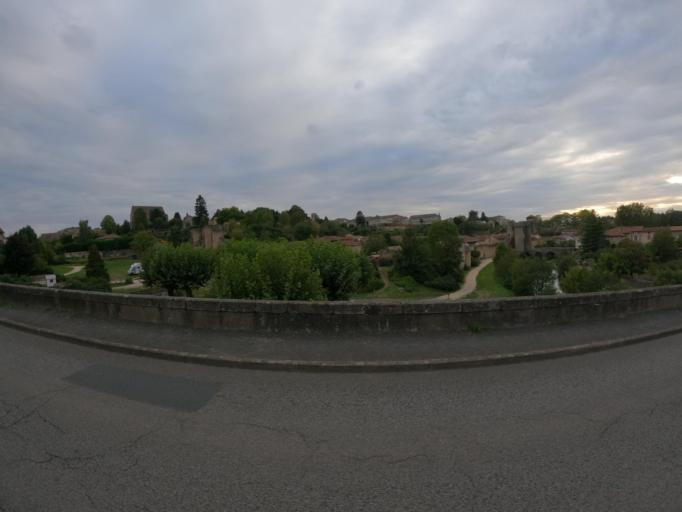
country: FR
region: Poitou-Charentes
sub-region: Departement des Deux-Sevres
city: Parthenay
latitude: 46.6524
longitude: -0.2470
